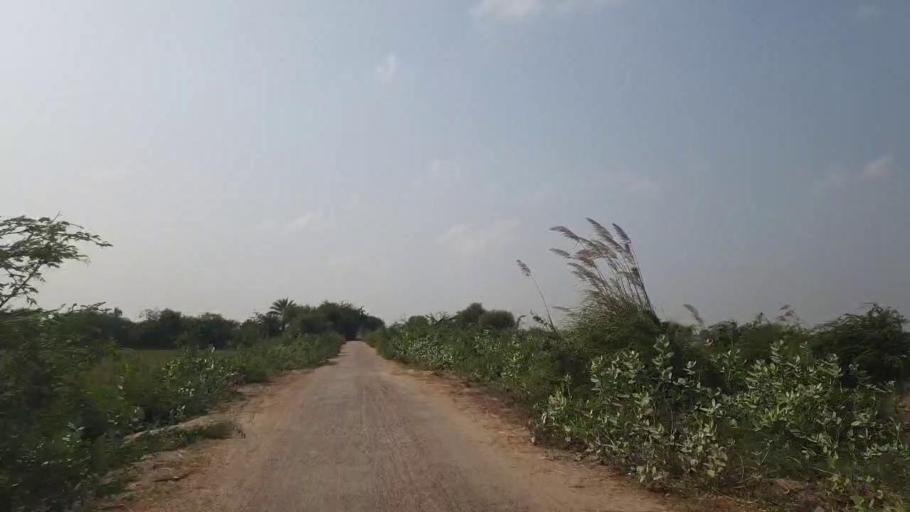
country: PK
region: Sindh
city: Badin
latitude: 24.7442
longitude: 68.7433
